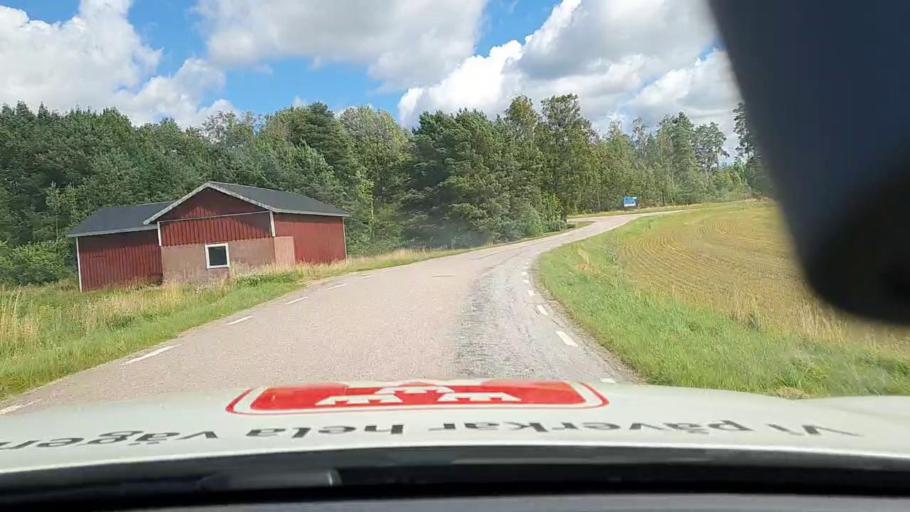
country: SE
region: Vaestra Goetaland
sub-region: Toreboda Kommun
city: Toereboda
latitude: 58.5836
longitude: 14.1196
